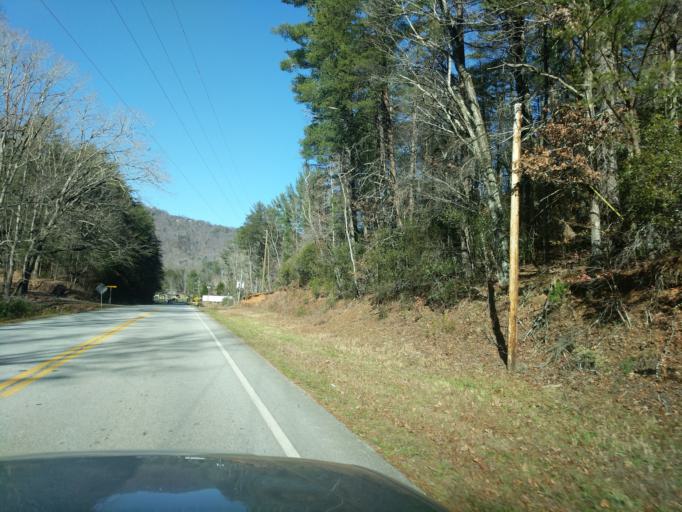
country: US
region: Georgia
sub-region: Rabun County
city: Clayton
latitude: 34.8495
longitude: -83.3618
